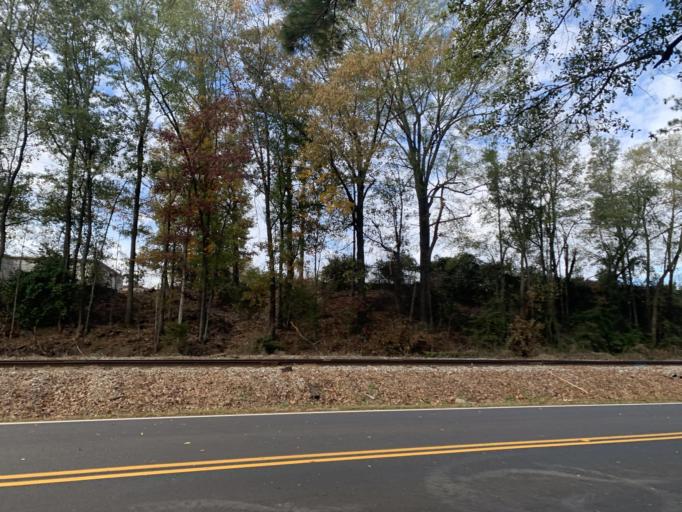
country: US
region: South Carolina
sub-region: Greenville County
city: Mauldin
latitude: 34.7814
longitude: -82.3086
